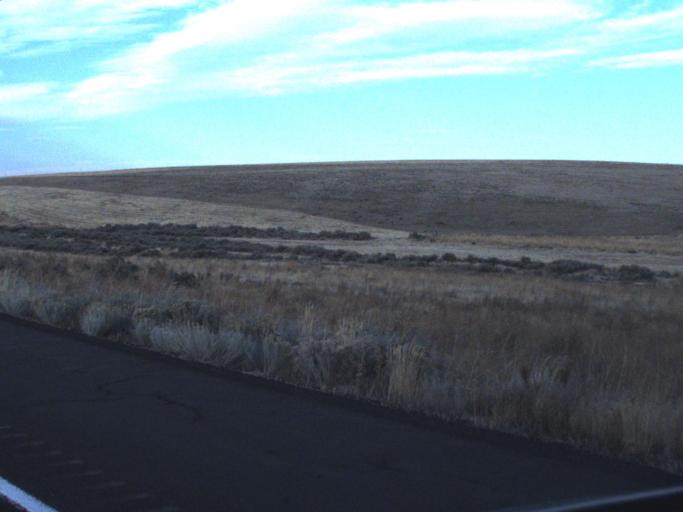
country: US
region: Washington
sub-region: Franklin County
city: Connell
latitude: 46.8034
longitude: -118.7287
